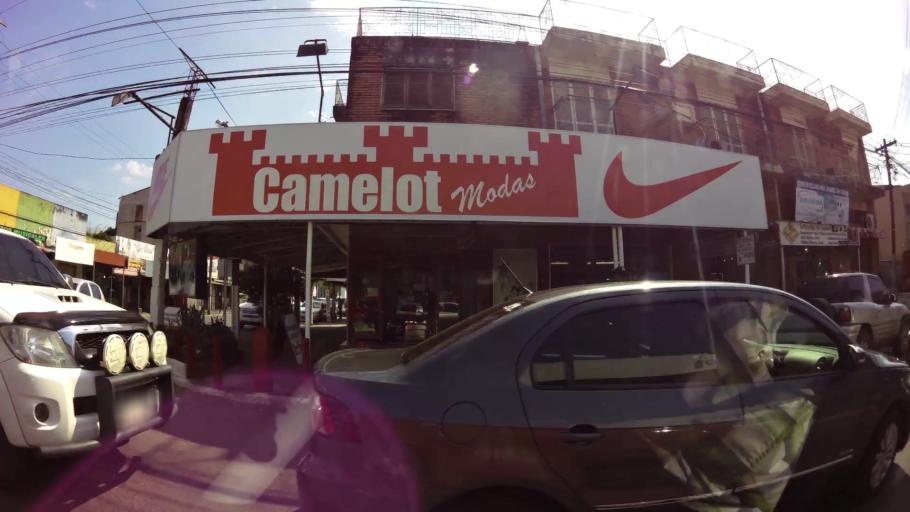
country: PY
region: Central
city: San Lorenzo
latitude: -25.3486
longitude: -57.5125
